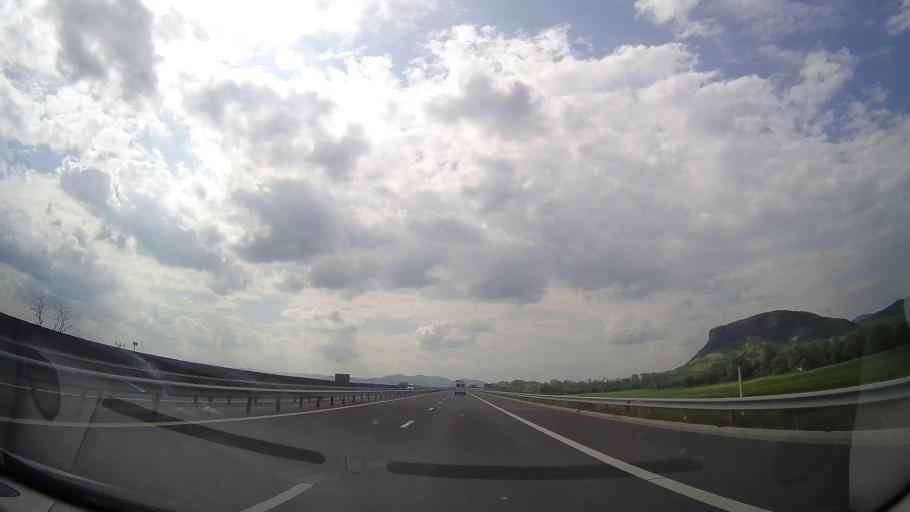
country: RO
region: Hunedoara
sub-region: Comuna Rapoltu Mare
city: Rapoltu Mare
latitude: 45.8471
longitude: 23.0580
